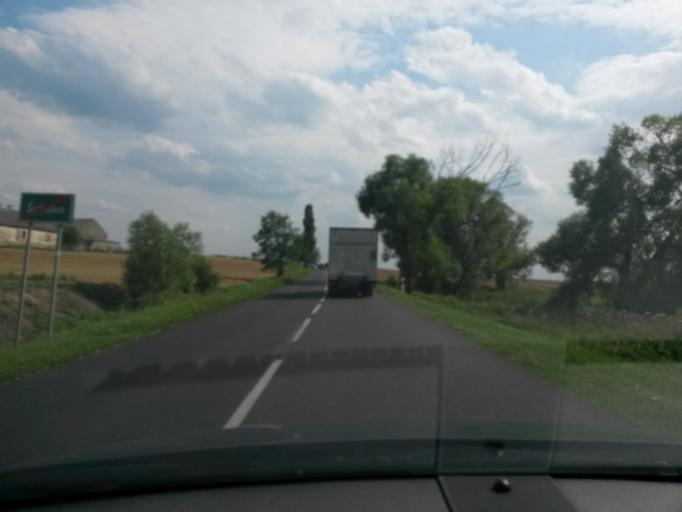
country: PL
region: Greater Poland Voivodeship
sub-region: Powiat poznanski
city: Kleszczewo
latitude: 52.2990
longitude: 17.1228
